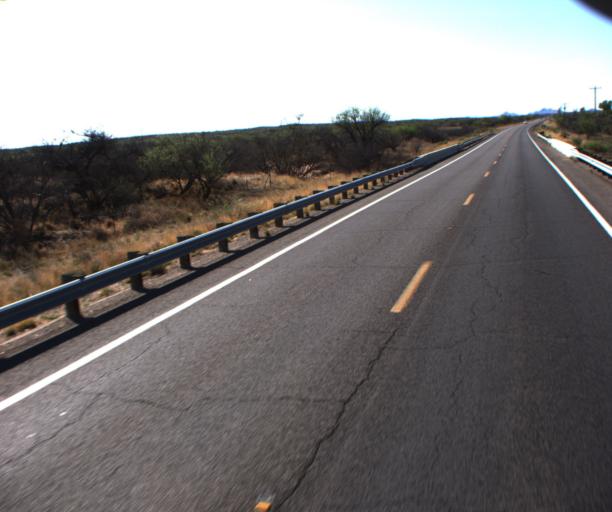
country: US
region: Arizona
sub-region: Cochise County
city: Saint David
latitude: 31.8626
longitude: -110.2050
